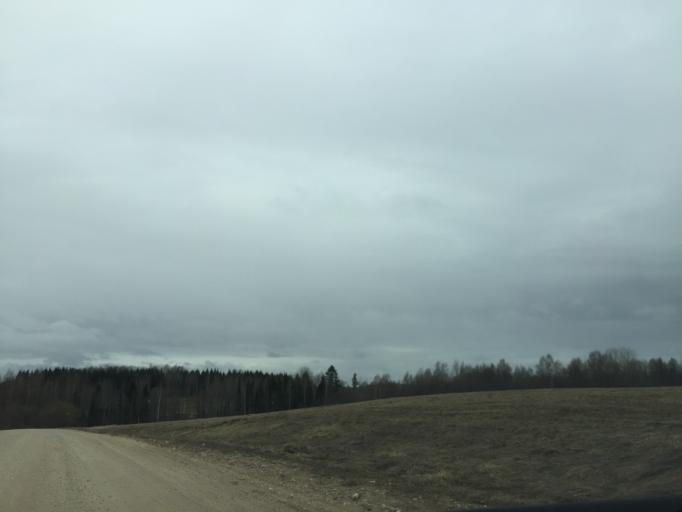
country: LV
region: Kraslavas Rajons
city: Kraslava
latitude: 55.9840
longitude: 27.1261
